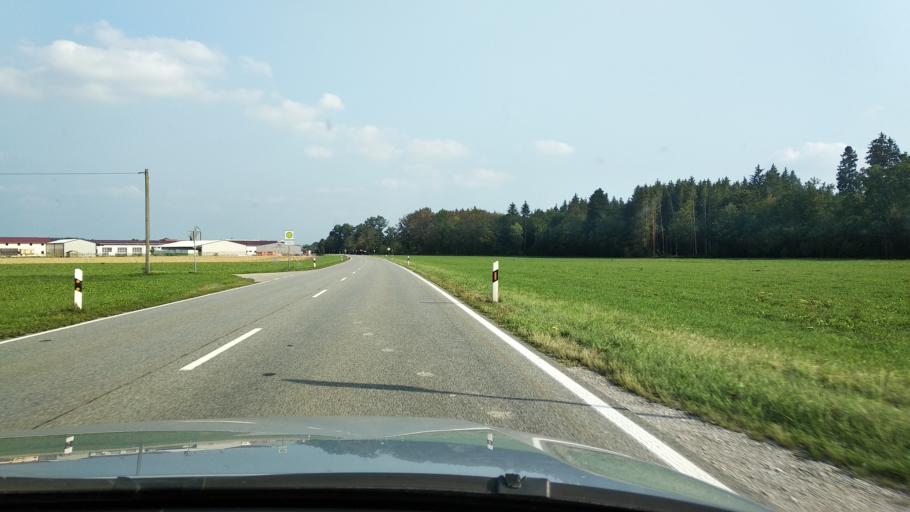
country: DE
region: Bavaria
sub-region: Upper Bavaria
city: Edling
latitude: 48.0709
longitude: 12.1439
